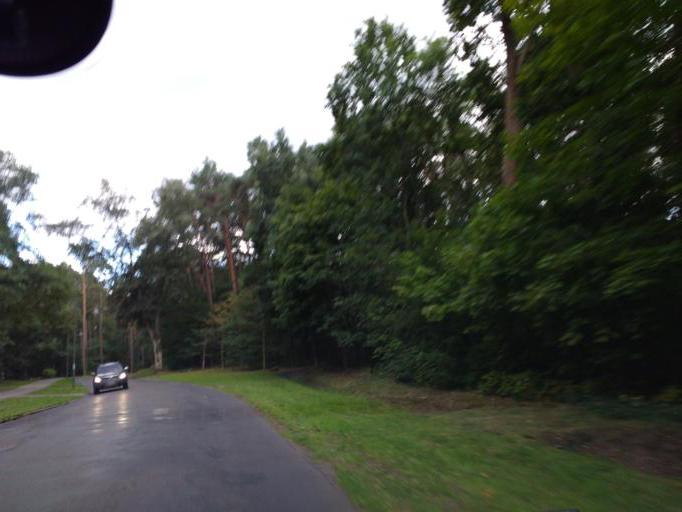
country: DE
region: Brandenburg
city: Bad Saarow
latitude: 52.2788
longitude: 14.0392
